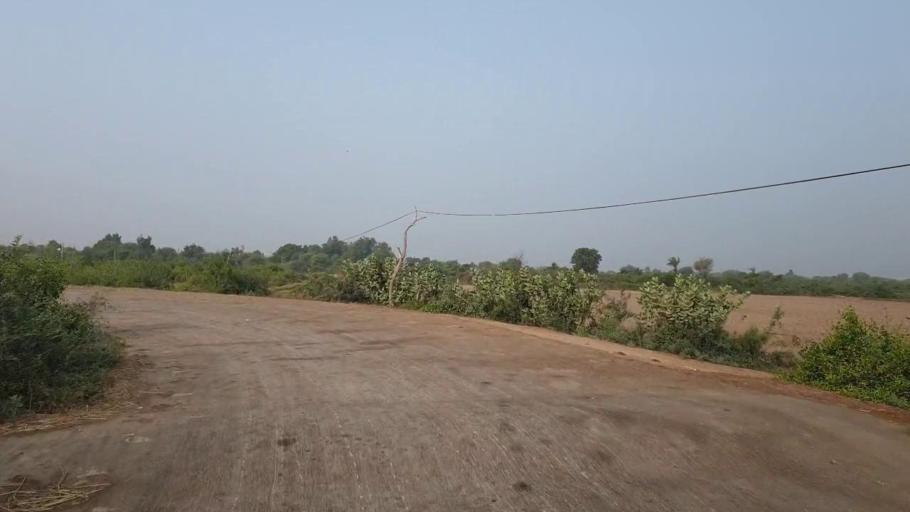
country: PK
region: Sindh
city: Tando Muhammad Khan
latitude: 25.1464
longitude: 68.6041
